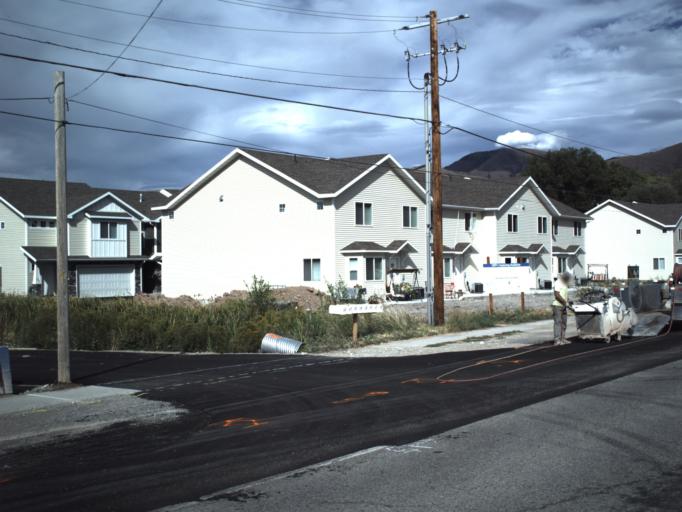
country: US
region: Utah
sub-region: Cache County
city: Hyrum
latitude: 41.6342
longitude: -111.8637
